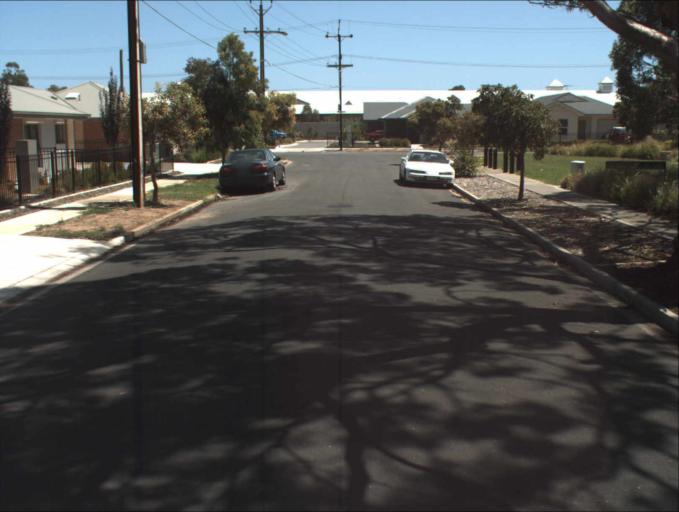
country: AU
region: South Australia
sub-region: Charles Sturt
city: Woodville North
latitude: -34.8549
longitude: 138.5590
